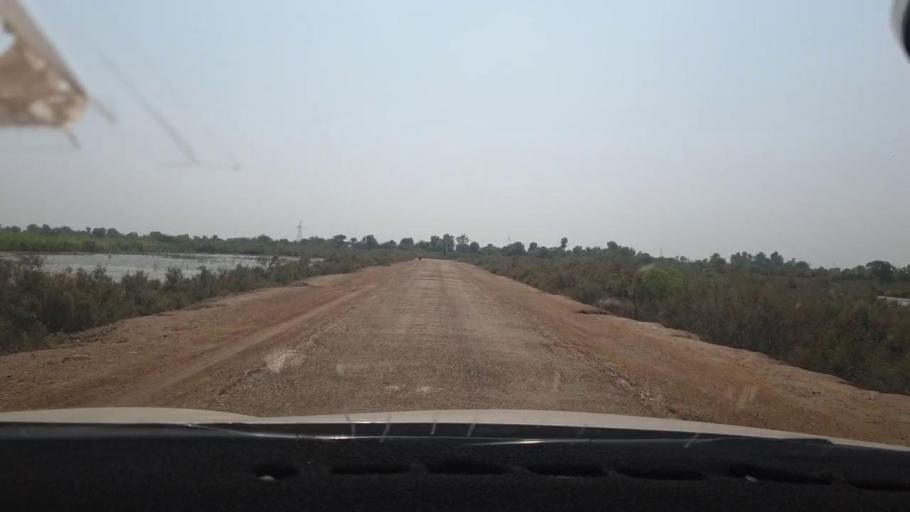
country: PK
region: Sindh
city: Tando Mittha Khan
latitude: 25.9227
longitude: 69.2338
